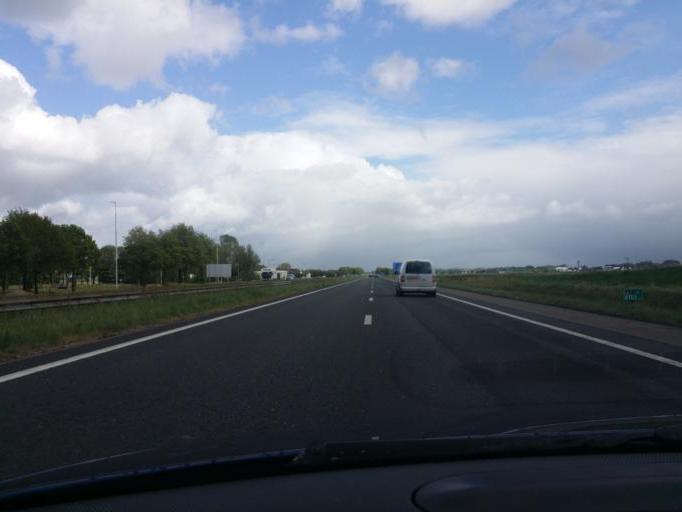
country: NL
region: Groningen
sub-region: Gemeente Hoogezand-Sappemeer
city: Hoogezand
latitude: 53.1885
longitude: 6.7125
